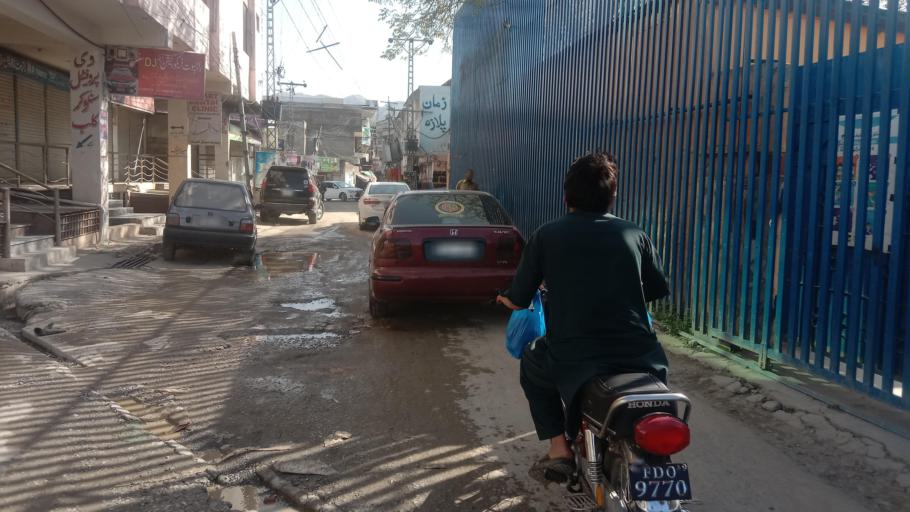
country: PK
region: Khyber Pakhtunkhwa
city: Abbottabad
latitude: 34.1711
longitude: 73.2231
